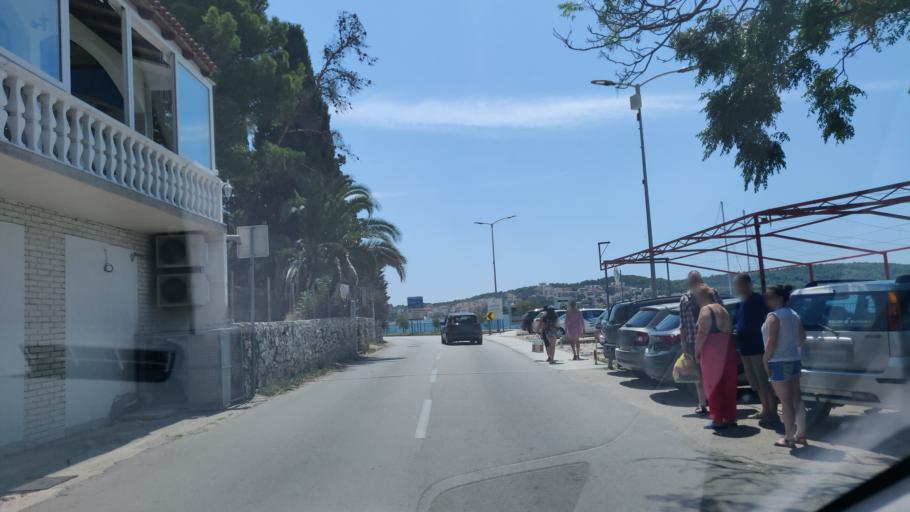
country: HR
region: Splitsko-Dalmatinska
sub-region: Grad Trogir
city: Trogir
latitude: 43.5041
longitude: 16.2580
